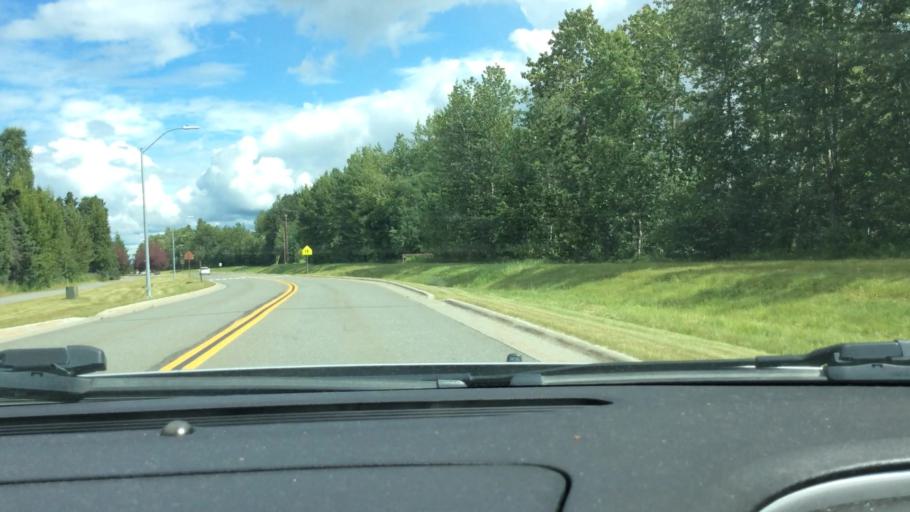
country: US
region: Alaska
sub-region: Anchorage Municipality
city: Anchorage
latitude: 61.2369
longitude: -149.8683
